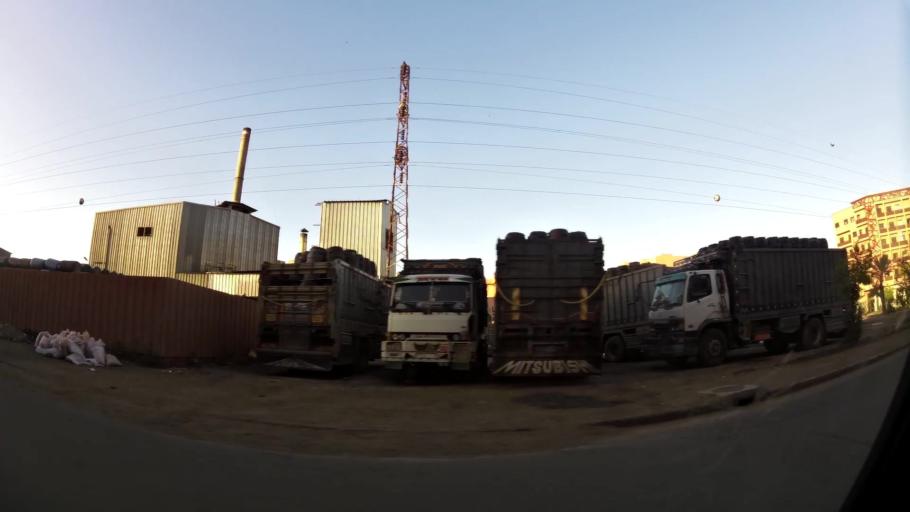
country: MA
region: Marrakech-Tensift-Al Haouz
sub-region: Marrakech
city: Marrakesh
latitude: 31.6242
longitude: -8.0304
